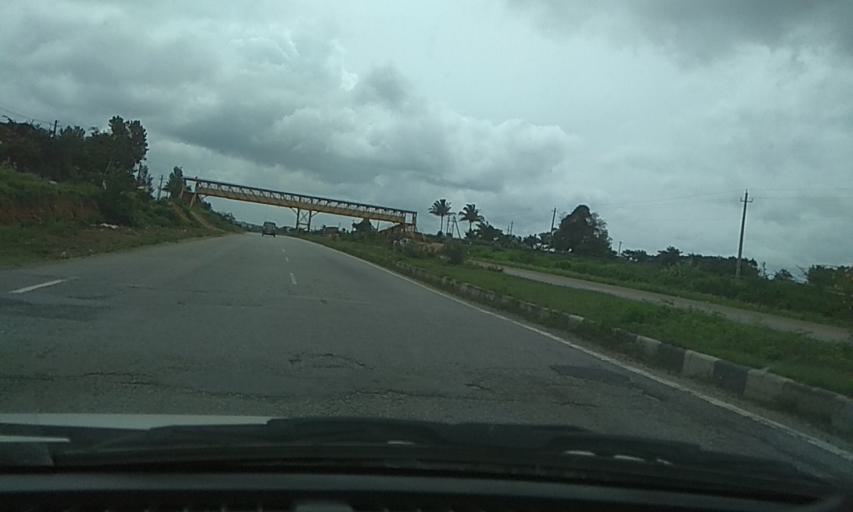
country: IN
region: Karnataka
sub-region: Davanagere
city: Mayakonda
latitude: 14.3671
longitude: 76.1491
